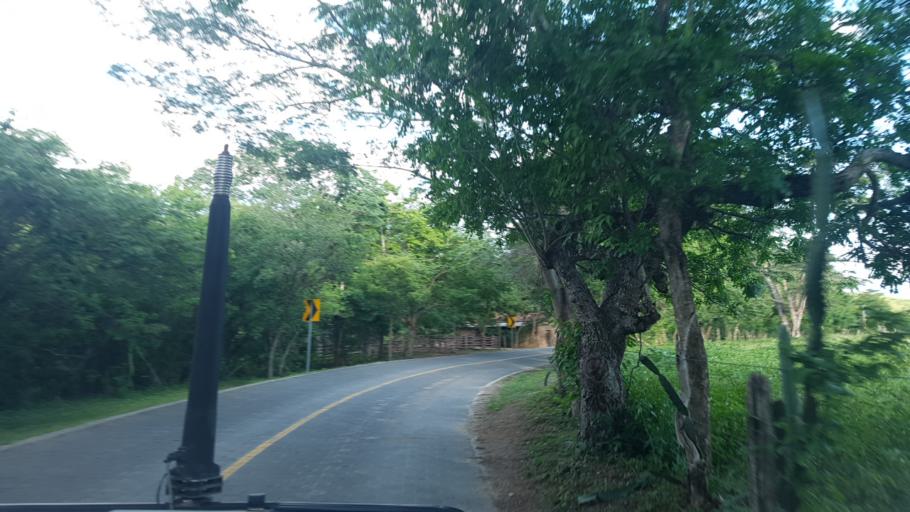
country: NI
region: Nueva Segovia
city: Ocotal
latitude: 13.6444
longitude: -86.5949
